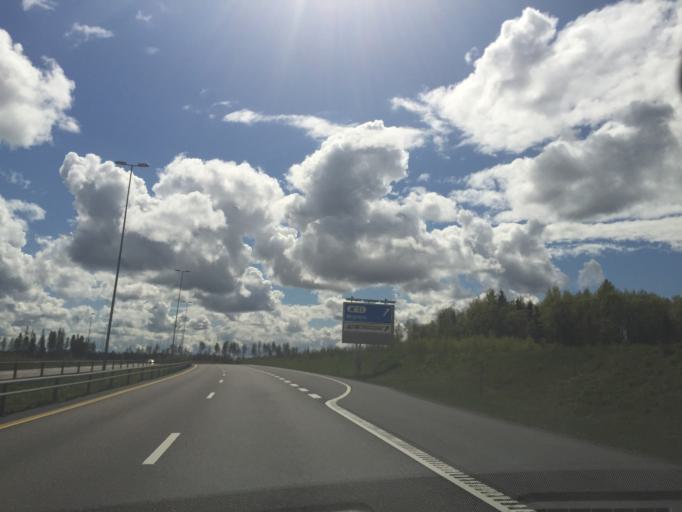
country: NO
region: Akershus
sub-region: Eidsvoll
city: Raholt
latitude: 60.2344
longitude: 11.1742
